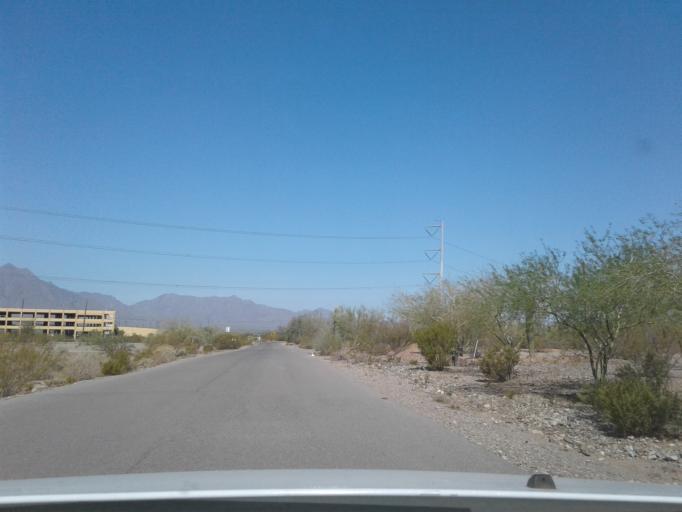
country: US
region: Arizona
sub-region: Maricopa County
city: Laveen
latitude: 33.3122
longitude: -112.1537
